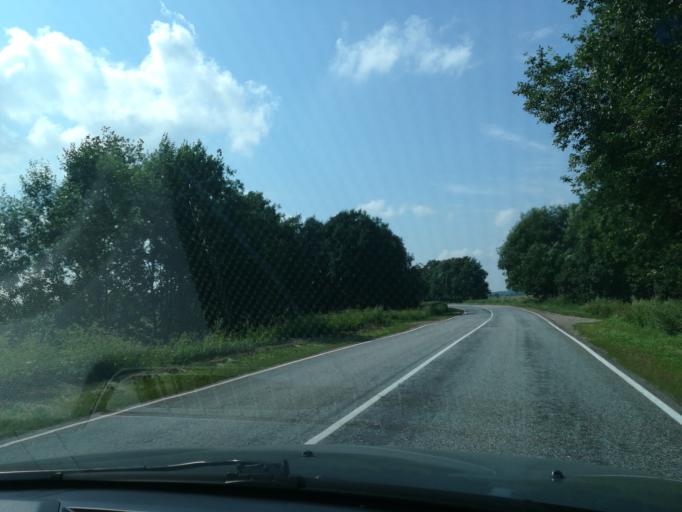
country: RU
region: Leningrad
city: Kopor'ye
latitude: 59.7251
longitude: 29.1051
